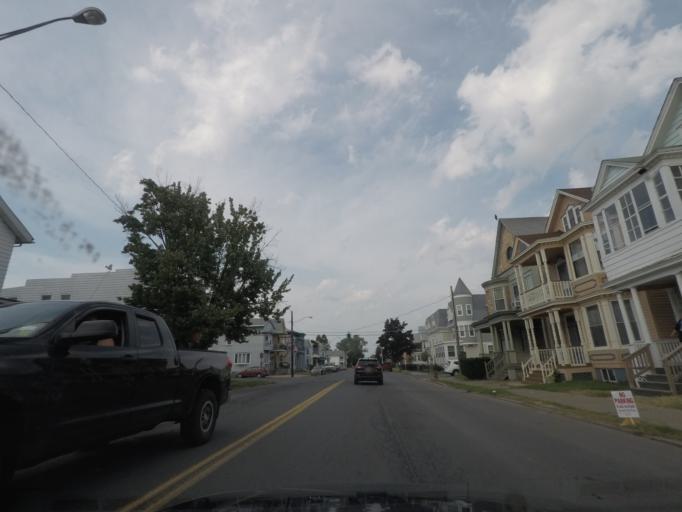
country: US
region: New York
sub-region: Albany County
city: Green Island
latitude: 42.7610
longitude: -73.6796
